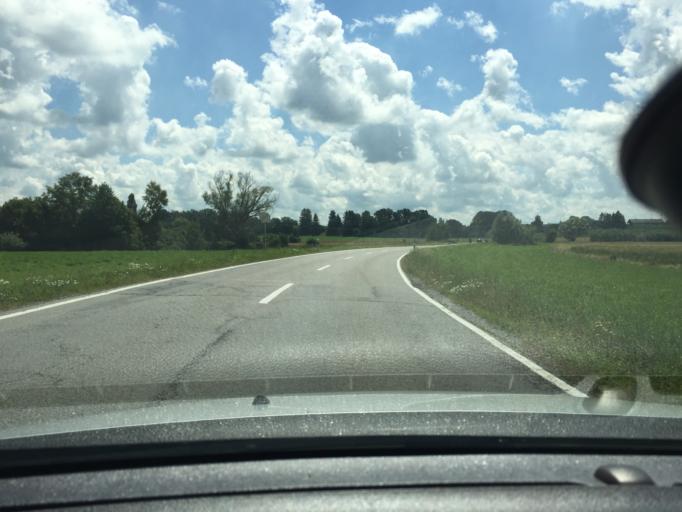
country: DE
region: Bavaria
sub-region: Upper Bavaria
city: Taufkirchen
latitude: 48.1434
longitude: 12.4517
